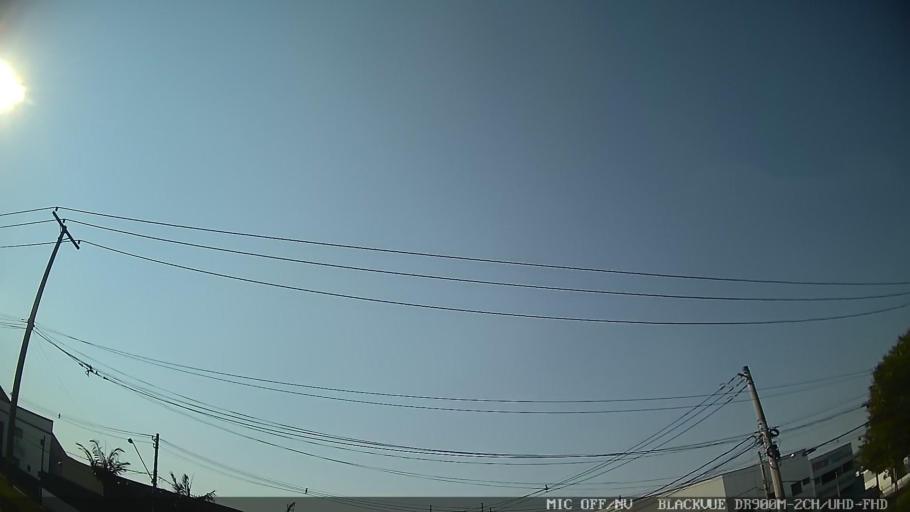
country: BR
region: Sao Paulo
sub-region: Itatiba
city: Itatiba
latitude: -22.9867
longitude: -46.8430
